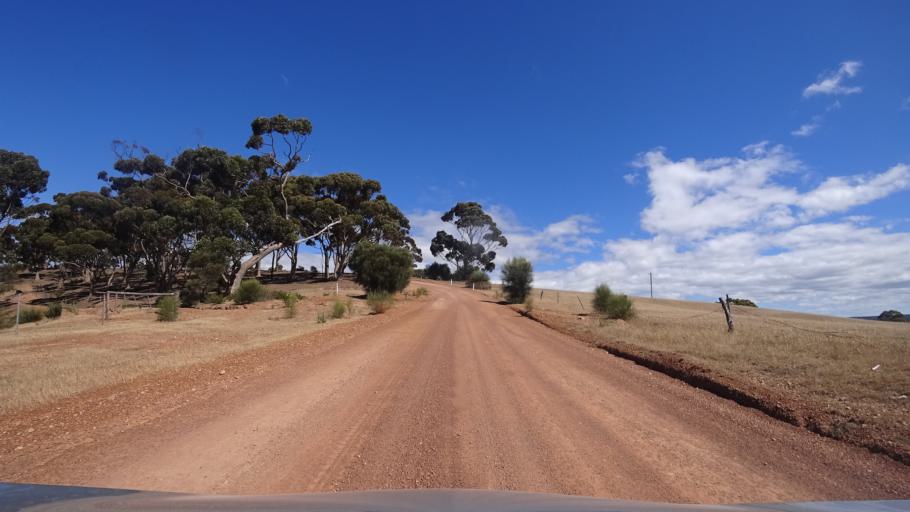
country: AU
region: South Australia
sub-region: Kangaroo Island
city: Kingscote
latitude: -35.6904
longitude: 136.9816
